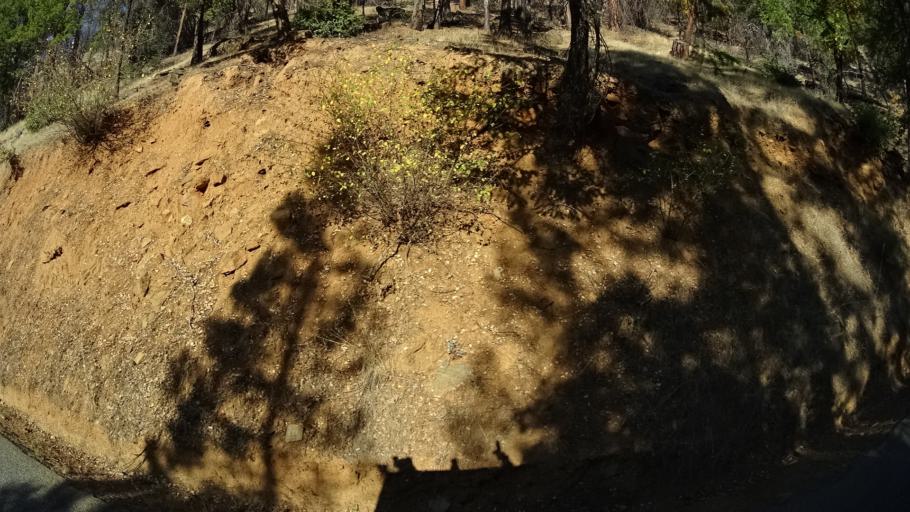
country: US
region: California
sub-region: Siskiyou County
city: Happy Camp
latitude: 41.7026
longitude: -123.0415
